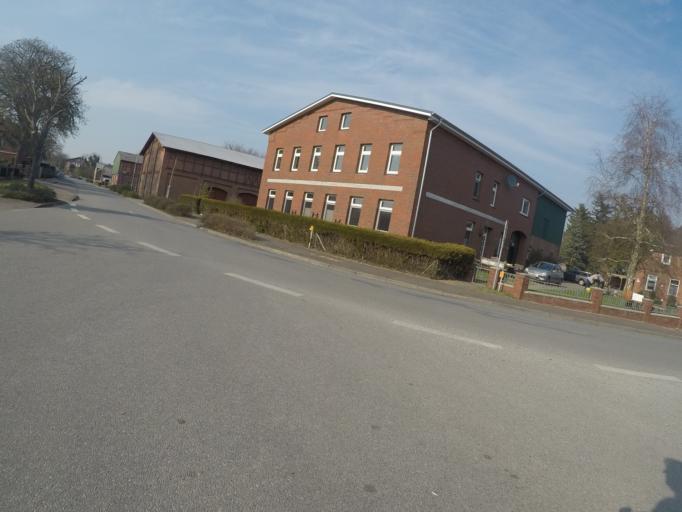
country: DE
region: Schleswig-Holstein
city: Kukels
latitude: 53.8948
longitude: 10.2390
